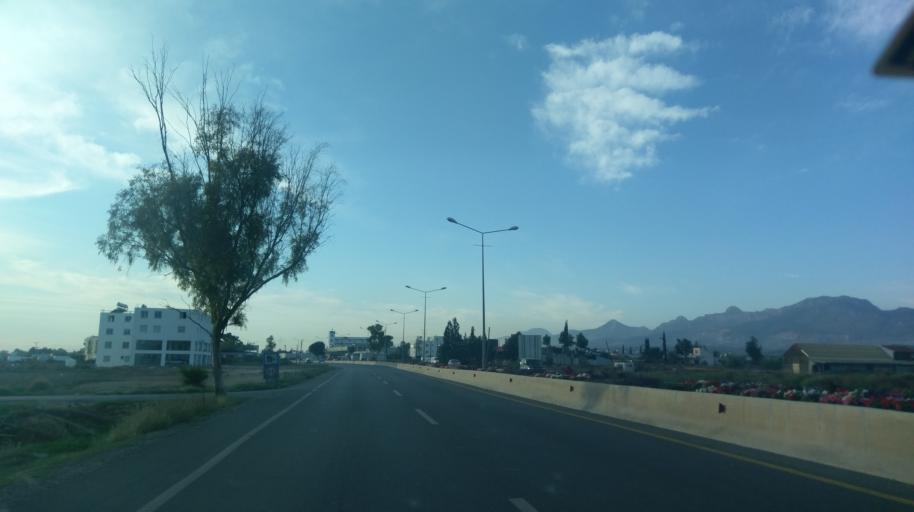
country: CY
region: Lefkosia
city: Nicosia
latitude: 35.2215
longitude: 33.4865
